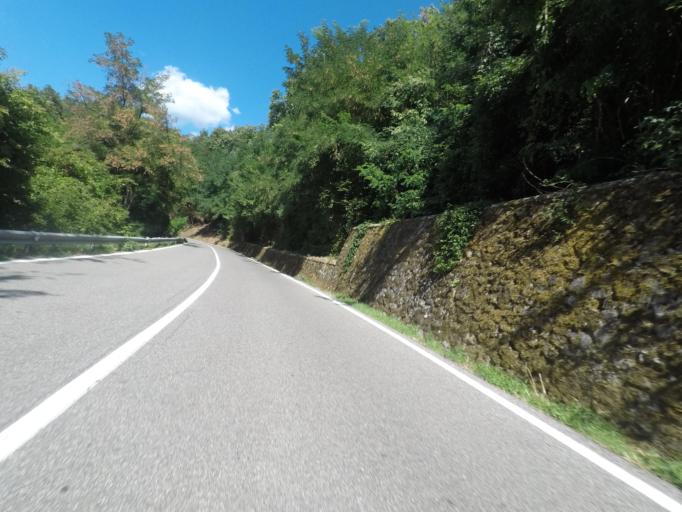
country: IT
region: Tuscany
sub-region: Provincia di Massa-Carrara
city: Fivizzano
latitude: 44.2423
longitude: 10.1584
